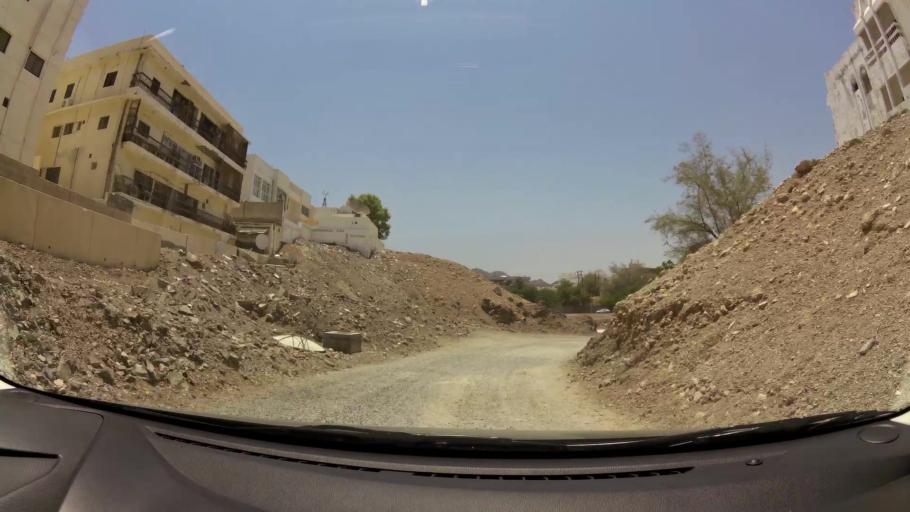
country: OM
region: Muhafazat Masqat
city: Muscat
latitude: 23.6095
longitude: 58.5375
